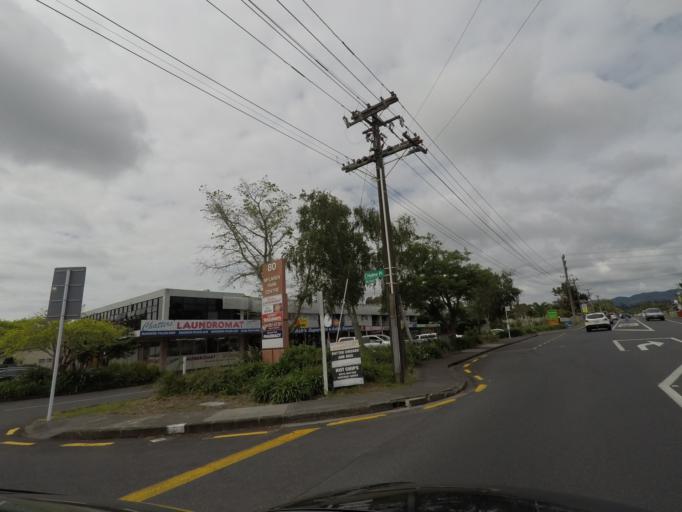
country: NZ
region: Auckland
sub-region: Auckland
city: Waitakere
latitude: -36.8963
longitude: 174.6268
